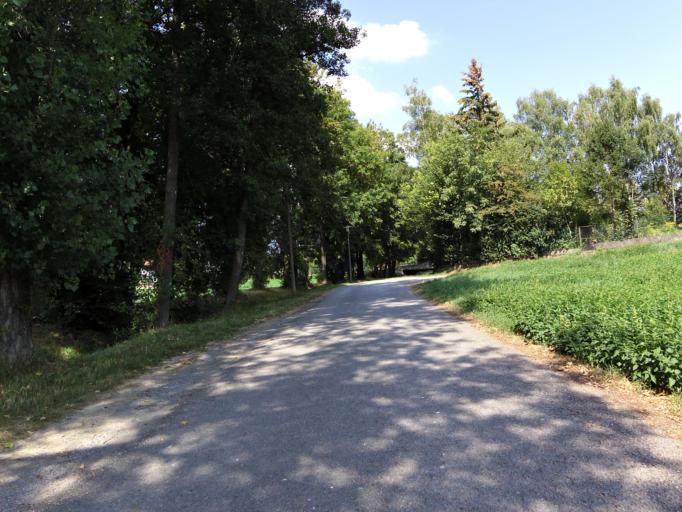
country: DE
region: Bavaria
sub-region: Regierungsbezirk Unterfranken
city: Estenfeld
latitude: 49.8320
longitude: 10.0124
